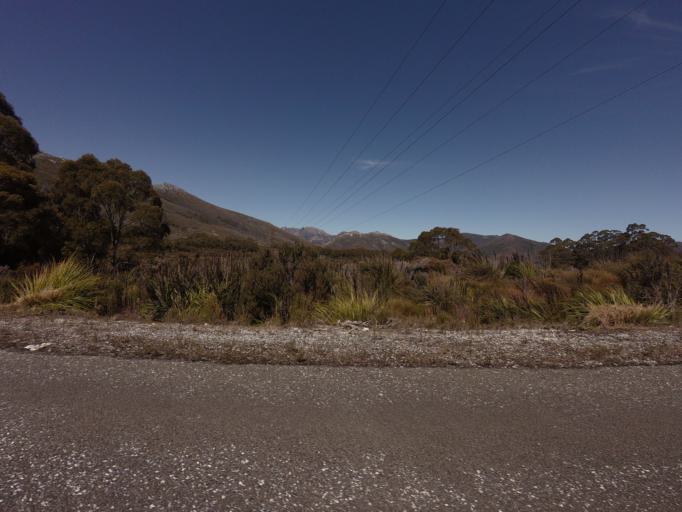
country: AU
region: Tasmania
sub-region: Huon Valley
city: Geeveston
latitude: -42.8344
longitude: 146.1466
